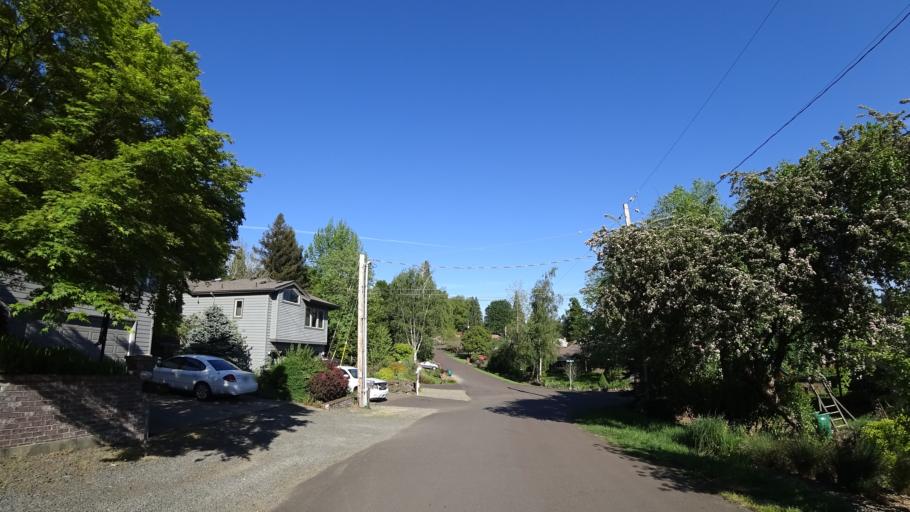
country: US
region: Oregon
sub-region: Washington County
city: West Slope
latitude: 45.4972
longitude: -122.7641
